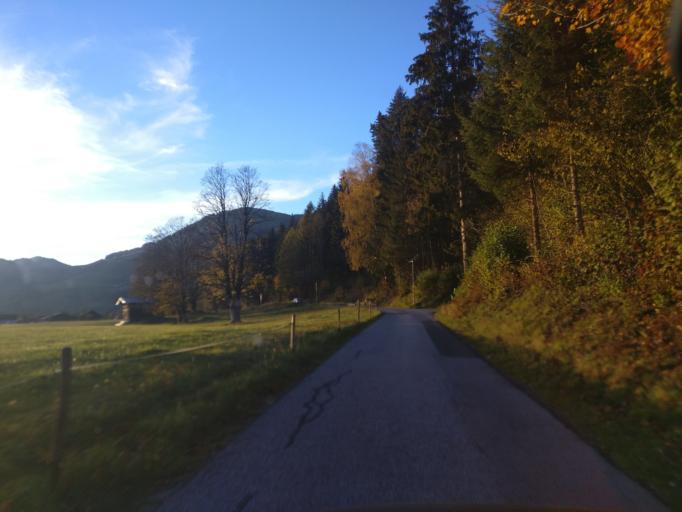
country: AT
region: Salzburg
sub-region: Politischer Bezirk Zell am See
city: Lend
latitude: 47.3157
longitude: 13.0422
